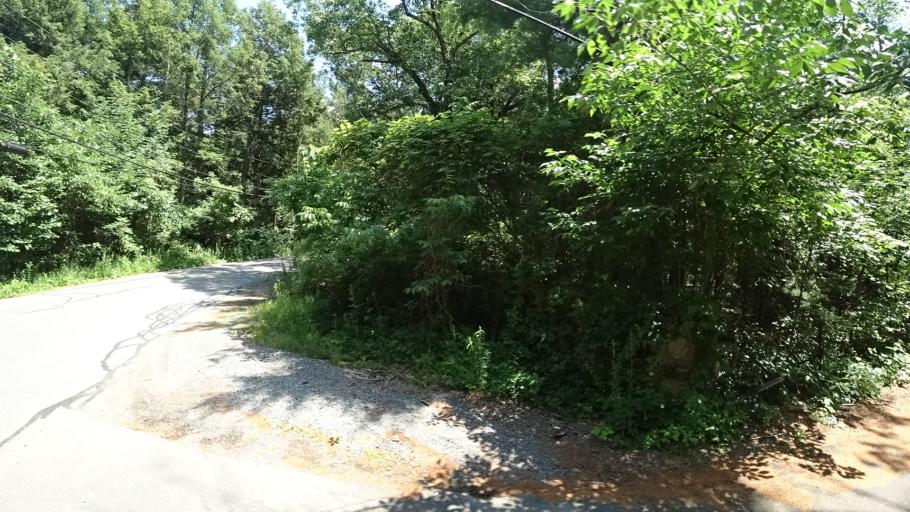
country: US
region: Massachusetts
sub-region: Norfolk County
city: Dedham
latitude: 42.2533
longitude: -71.1961
